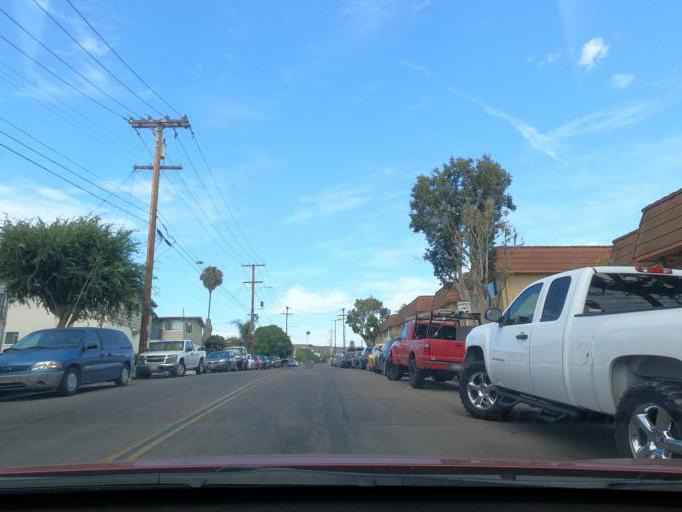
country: MX
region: Baja California
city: Tijuana
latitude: 32.5571
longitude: -117.0479
